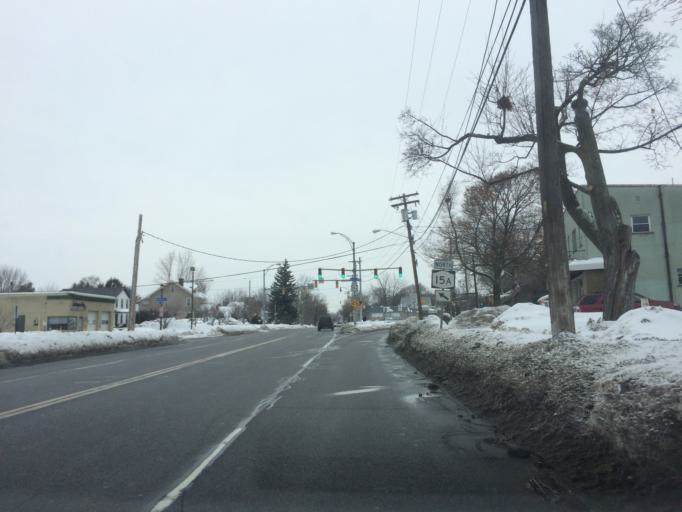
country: US
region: New York
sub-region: Monroe County
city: Rochester
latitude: 43.1161
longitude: -77.6166
